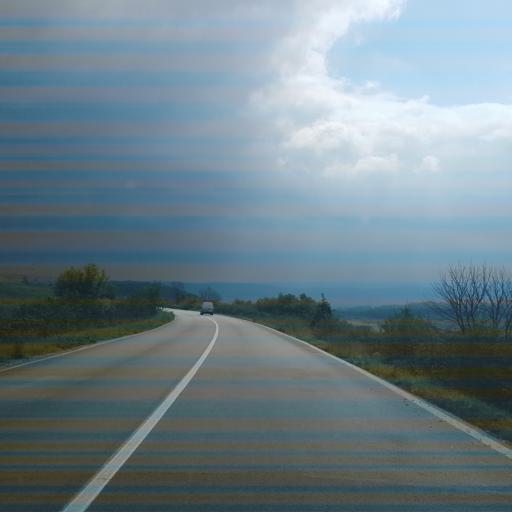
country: RS
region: Central Serbia
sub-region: Nisavski Okrug
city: Razanj
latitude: 43.6482
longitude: 21.5538
